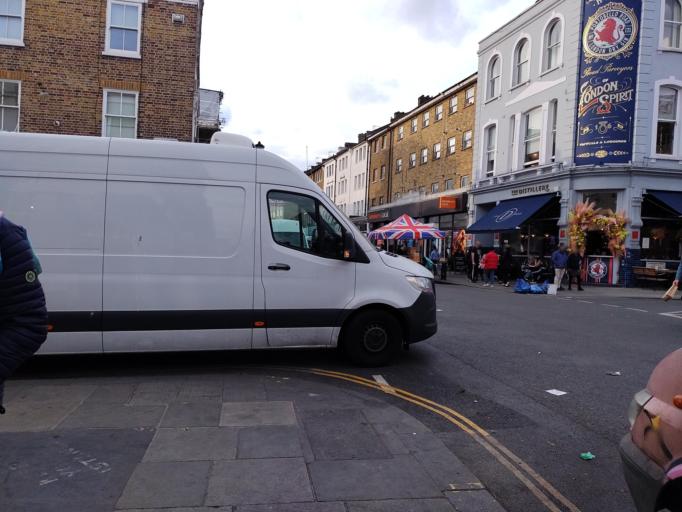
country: GB
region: England
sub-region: Greater London
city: Kensington
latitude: 51.5158
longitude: -0.2049
